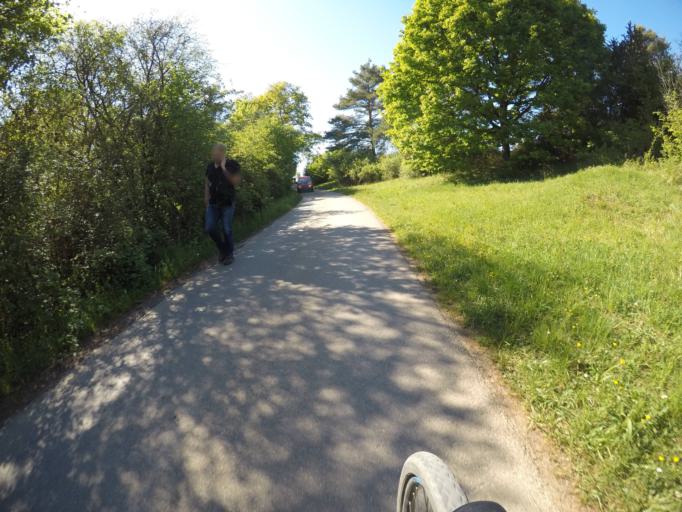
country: DE
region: Baden-Wuerttemberg
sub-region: Karlsruhe Region
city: Friolzheim
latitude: 48.8253
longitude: 8.8478
